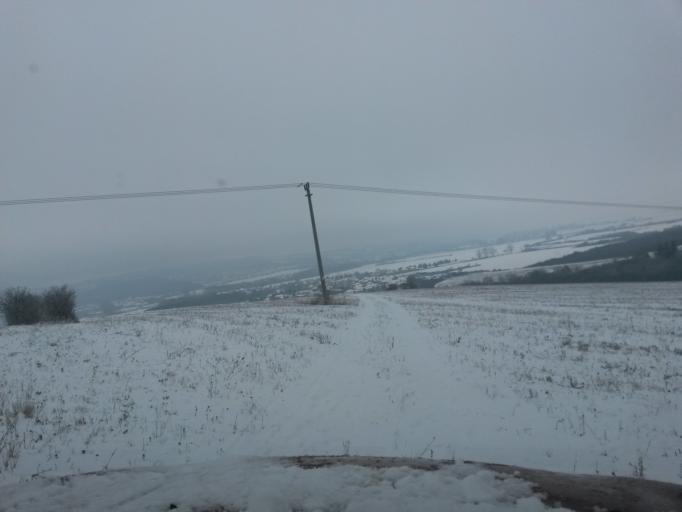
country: SK
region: Kosicky
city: Kosice
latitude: 48.7145
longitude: 21.3216
